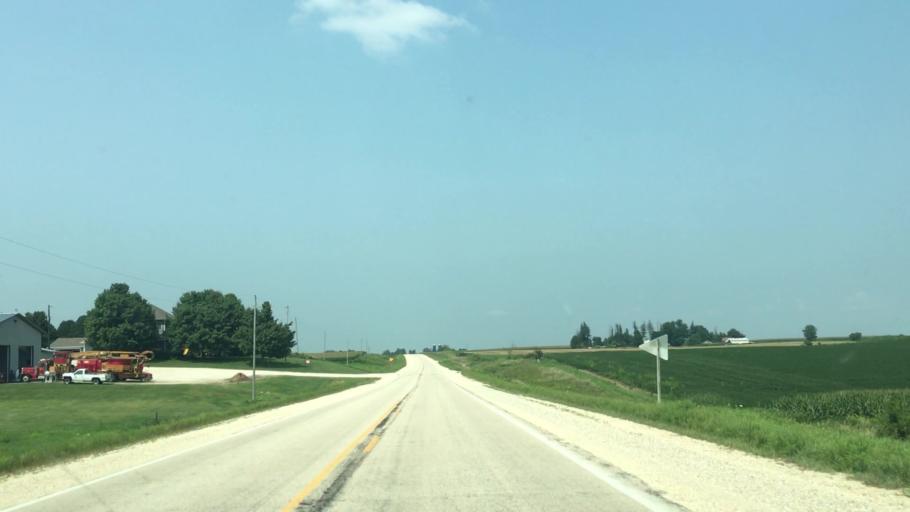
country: US
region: Iowa
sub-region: Fayette County
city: West Union
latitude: 42.9905
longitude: -91.8240
